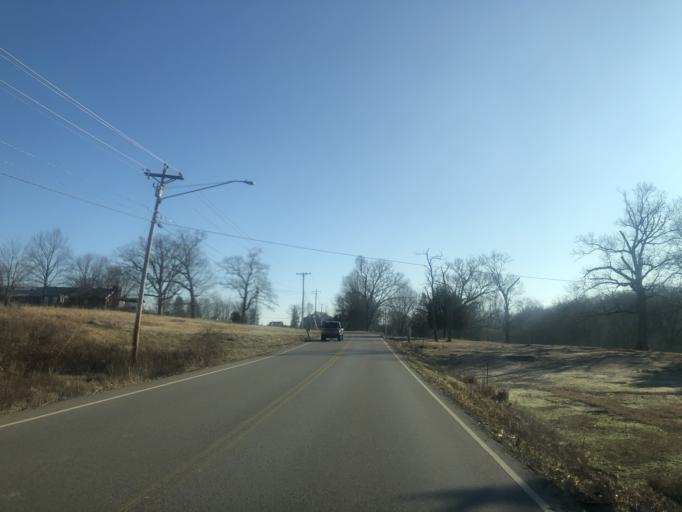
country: US
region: Tennessee
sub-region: Williamson County
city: Nolensville
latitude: 35.9654
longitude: -86.7049
